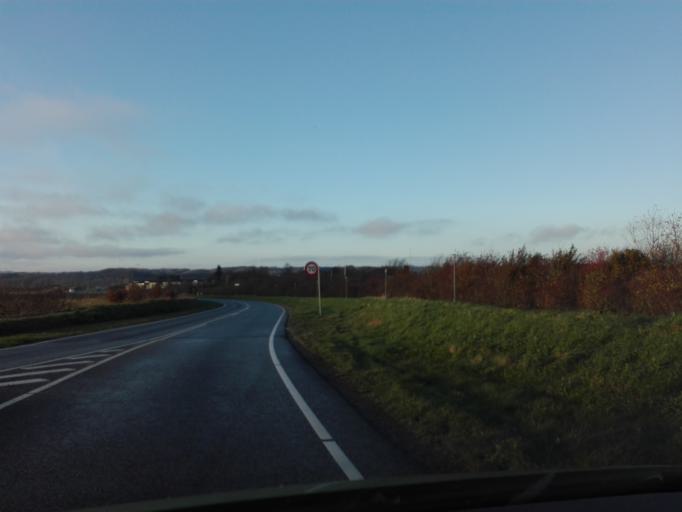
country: DK
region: Central Jutland
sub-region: Skanderborg Kommune
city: Stilling
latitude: 56.0513
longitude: 9.9808
